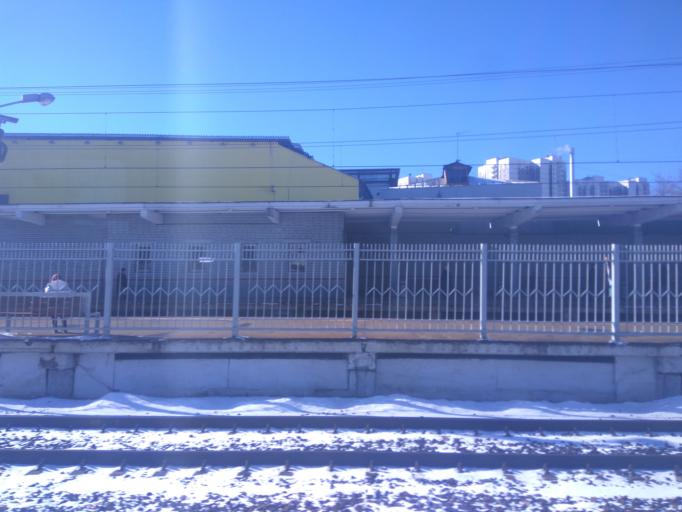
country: RU
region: Moscow
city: Taganskiy
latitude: 55.7487
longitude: 37.6805
